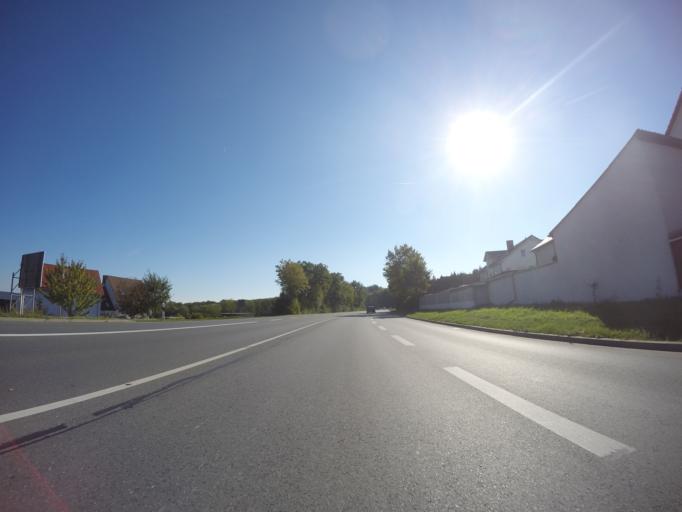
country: DE
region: Bavaria
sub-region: Regierungsbezirk Unterfranken
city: Waldbuttelbrunn
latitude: 49.7915
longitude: 9.8483
